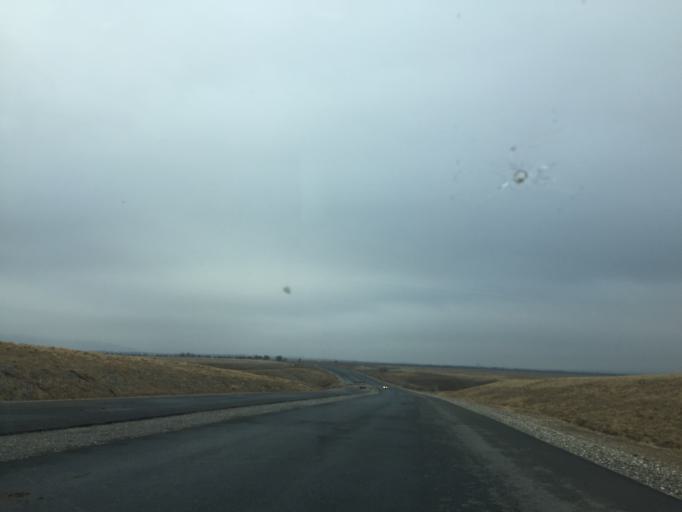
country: KZ
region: Ongtustik Qazaqstan
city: Kokterek
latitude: 42.5431
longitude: 70.1898
